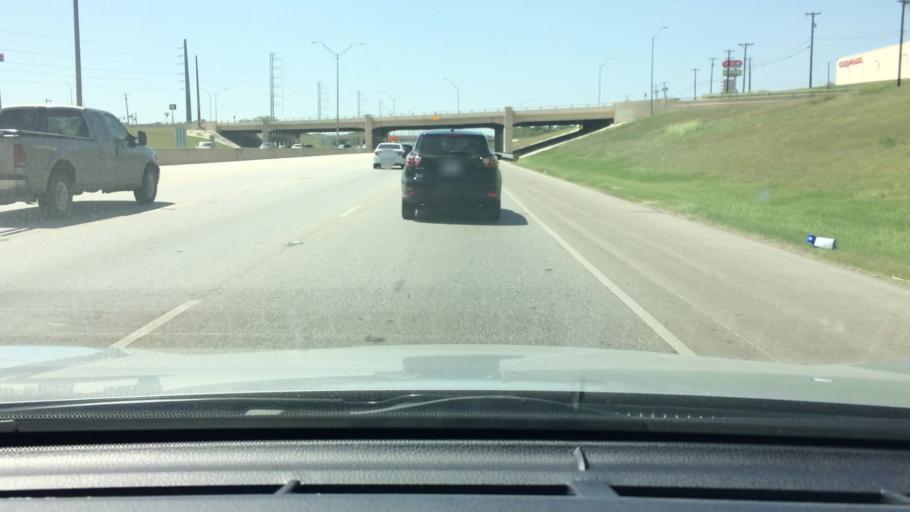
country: US
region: Texas
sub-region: Bexar County
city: San Antonio
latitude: 29.3743
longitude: -98.4578
